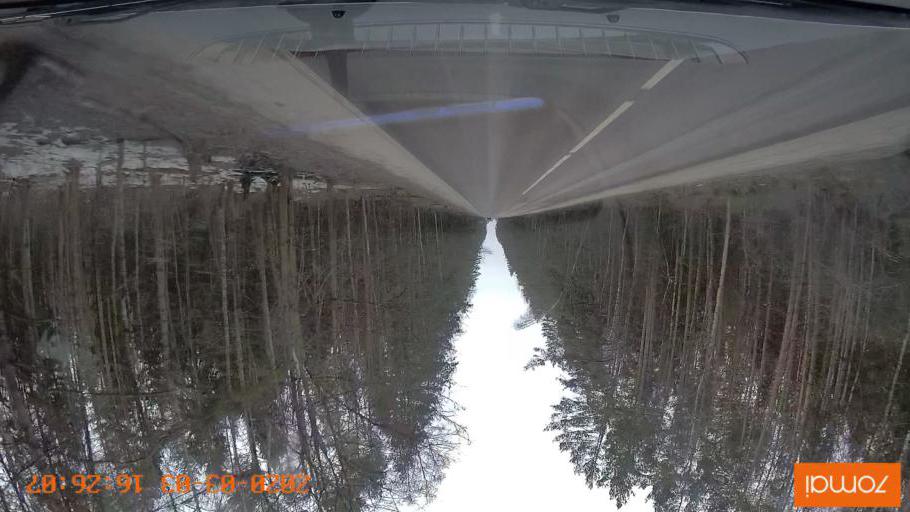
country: RU
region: Moskovskaya
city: Konobeyevo
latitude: 55.4429
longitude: 38.6602
